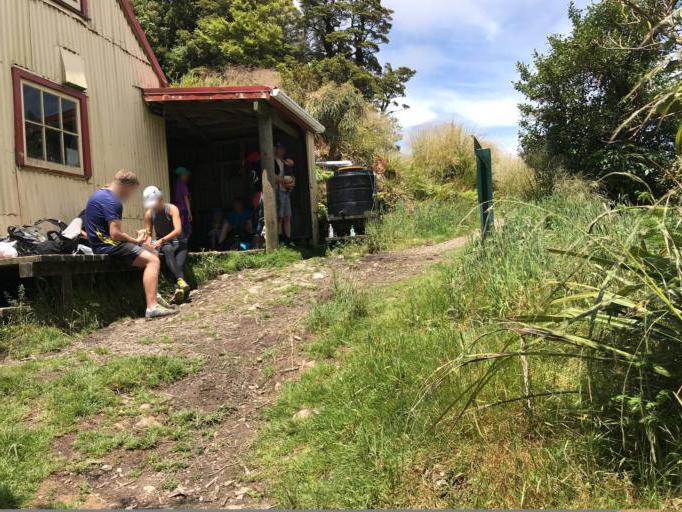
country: NZ
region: Wellington
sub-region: Kapiti Coast District
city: Otaki
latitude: -40.9077
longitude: 175.2561
